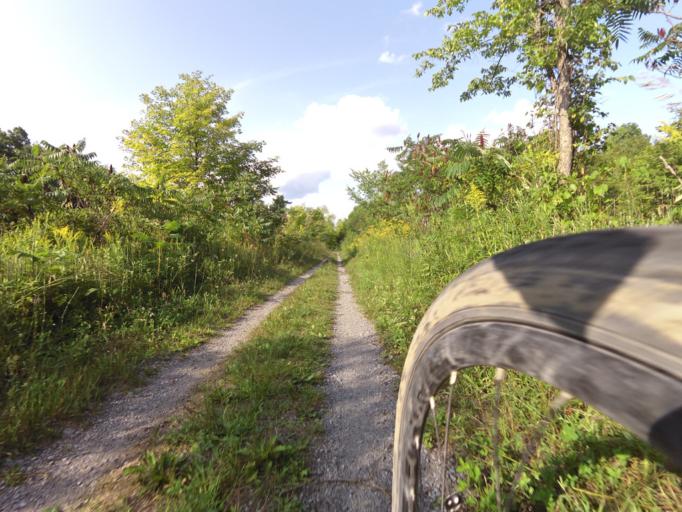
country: CA
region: Ontario
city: Kingston
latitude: 44.4490
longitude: -76.5250
